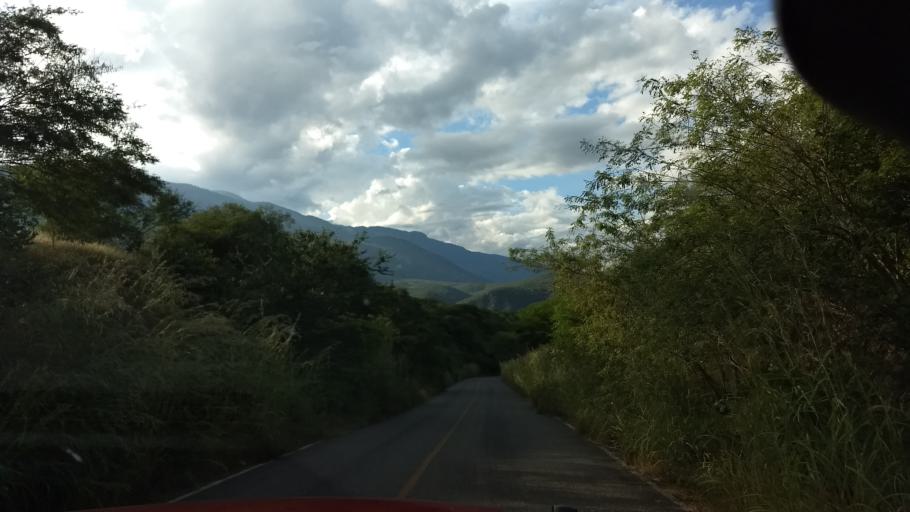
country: MX
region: Colima
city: Suchitlan
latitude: 19.4499
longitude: -103.8185
